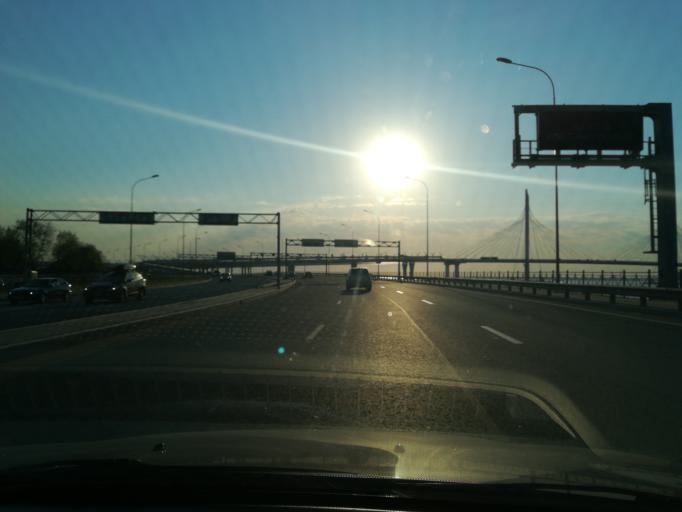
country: RU
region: St.-Petersburg
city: Staraya Derevnya
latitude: 59.9619
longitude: 30.2287
